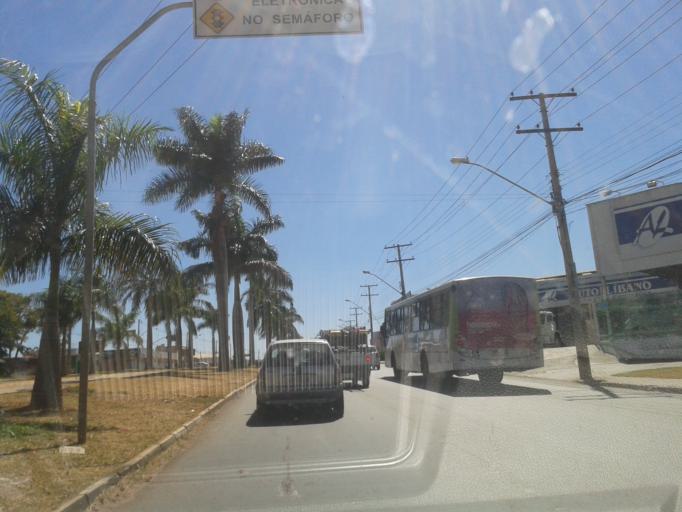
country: BR
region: Goias
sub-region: Goiania
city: Goiania
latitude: -16.6526
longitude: -49.2636
